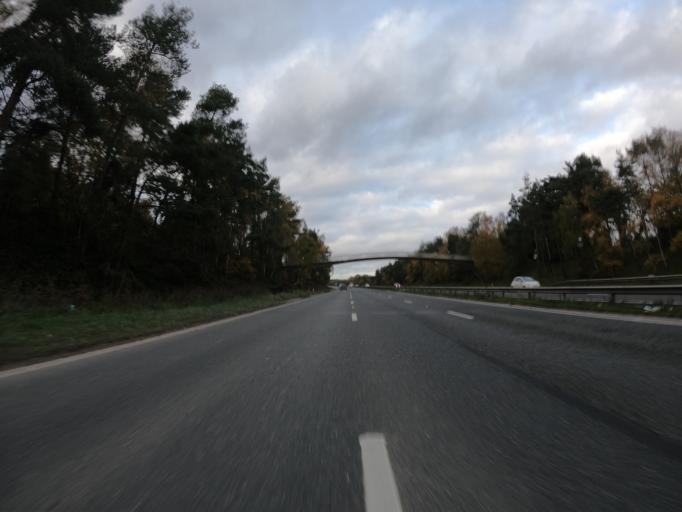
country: GB
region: England
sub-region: Kent
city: Swanley
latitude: 51.3996
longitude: 0.1579
